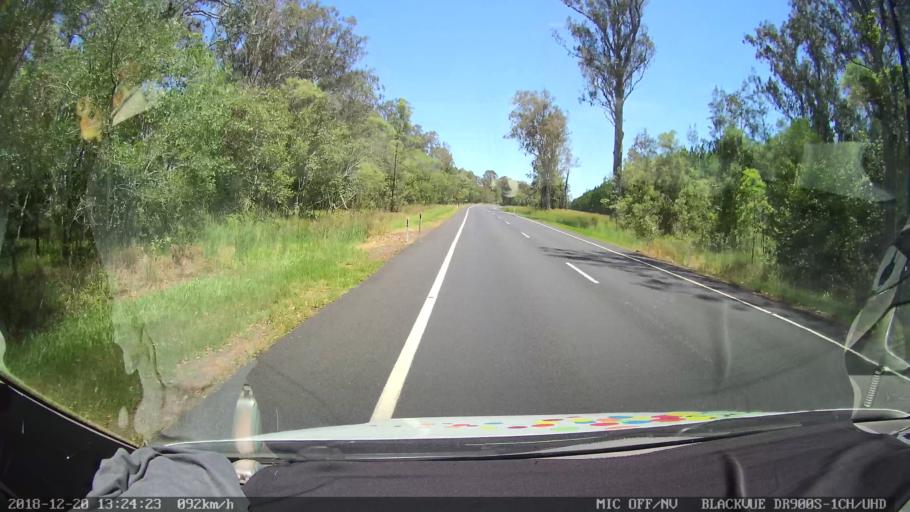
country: AU
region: New South Wales
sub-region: Richmond Valley
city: Casino
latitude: -29.1167
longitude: 153.0001
